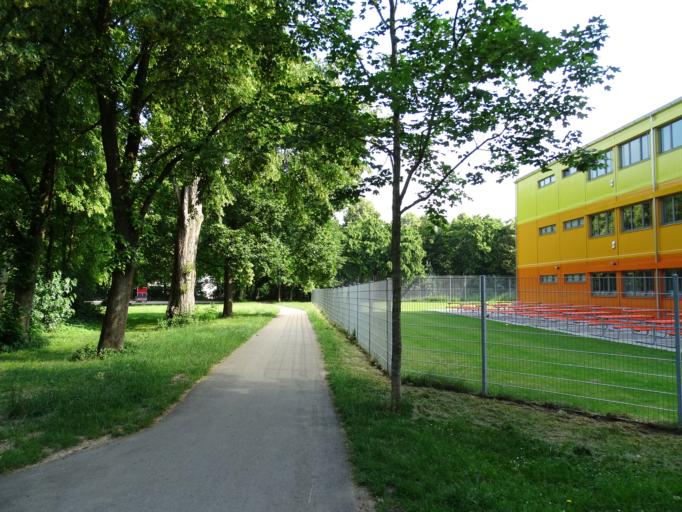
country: DE
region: Bavaria
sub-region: Upper Bavaria
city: Oberschleissheim
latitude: 48.2162
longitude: 11.5551
